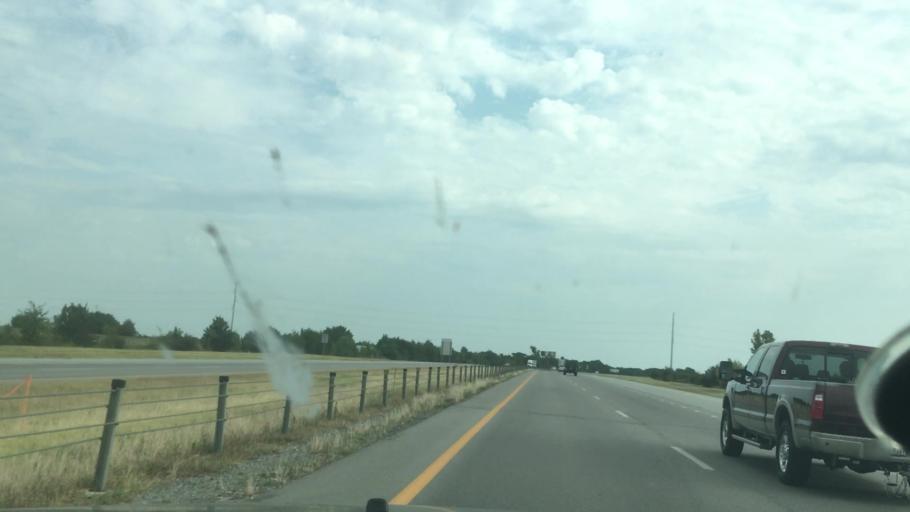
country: US
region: Oklahoma
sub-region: Bryan County
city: Calera
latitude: 33.9731
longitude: -96.4167
